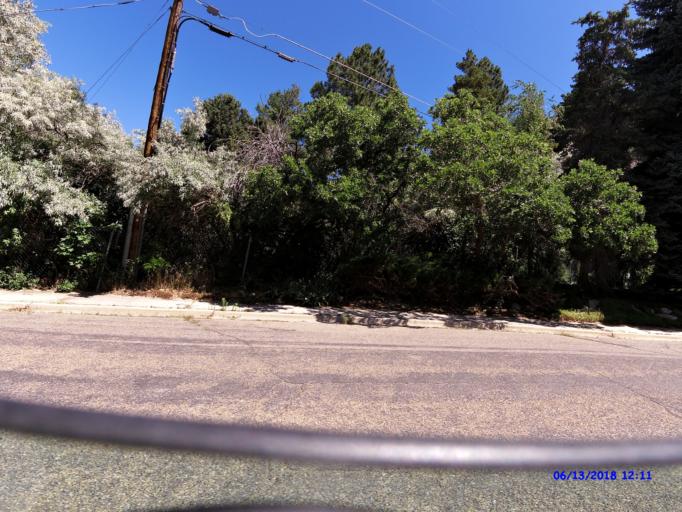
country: US
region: Utah
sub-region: Weber County
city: Ogden
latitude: 41.2149
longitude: -111.9307
